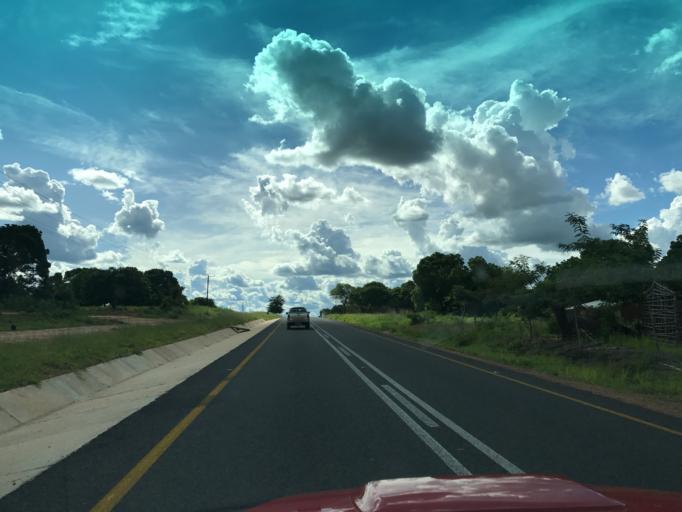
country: MZ
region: Nampula
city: Nampula
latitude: -15.0047
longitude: 38.9837
